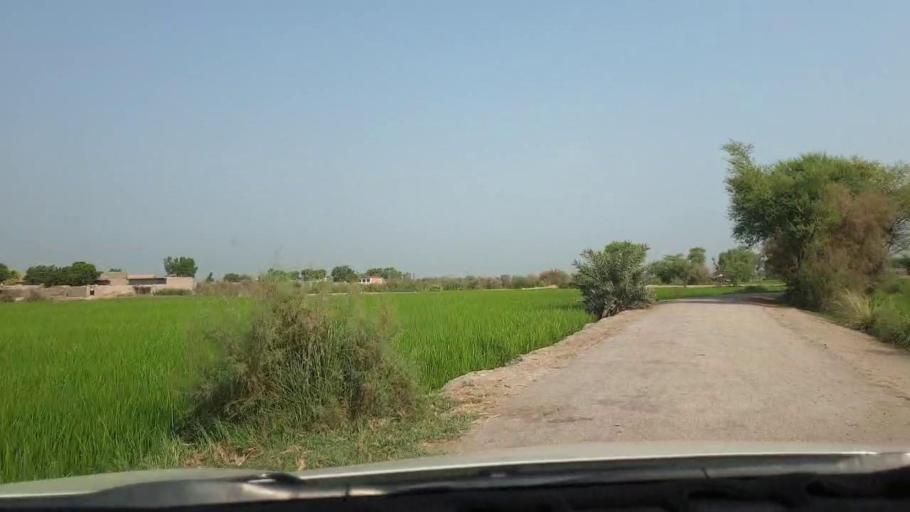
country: PK
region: Sindh
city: Goth Garelo
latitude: 27.4567
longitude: 68.1225
